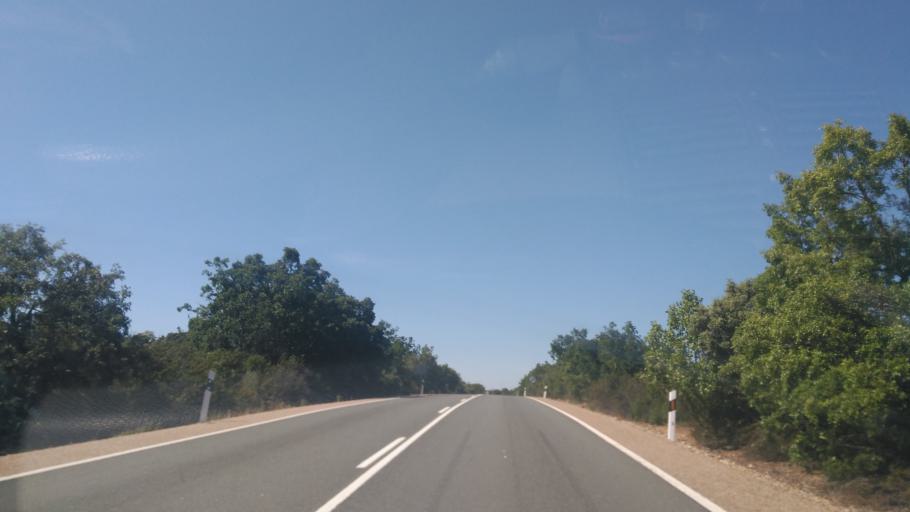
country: ES
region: Castille and Leon
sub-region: Provincia de Zamora
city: Cuelgamures
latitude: 41.2779
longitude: -5.7176
